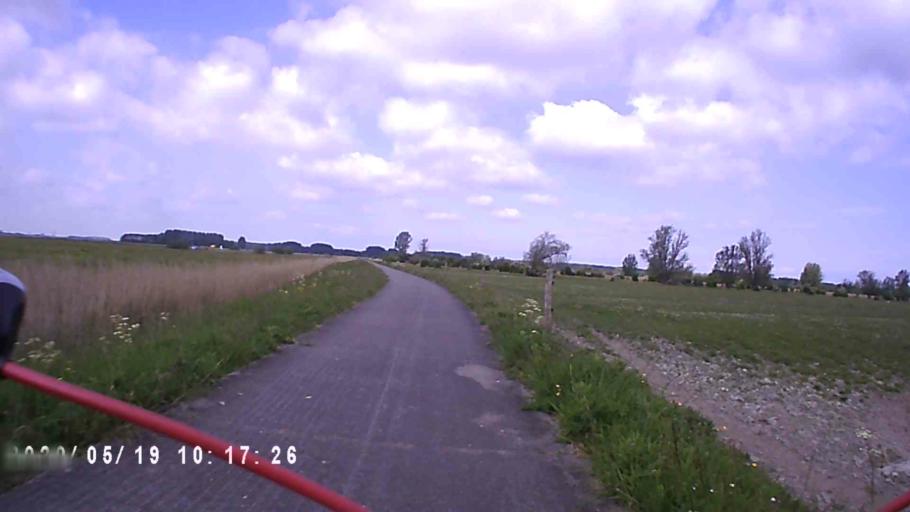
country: NL
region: Friesland
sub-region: Gemeente Kollumerland en Nieuwkruisland
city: Kollum
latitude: 53.3225
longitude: 6.2098
